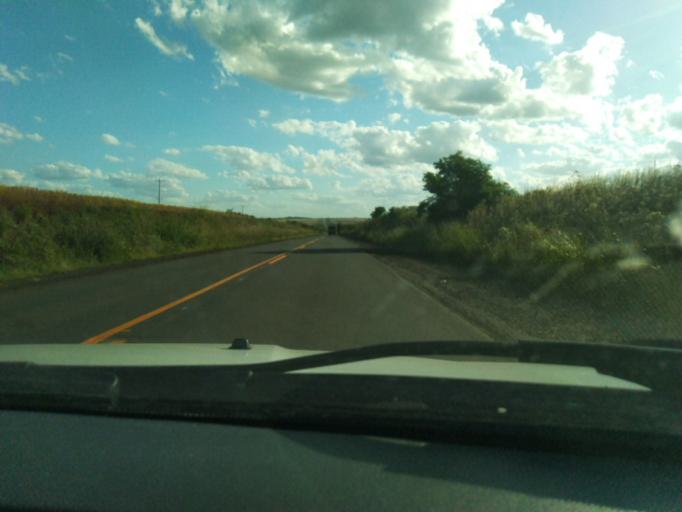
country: AR
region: Corrientes
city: Garruchos
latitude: -28.5526
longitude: -55.5699
